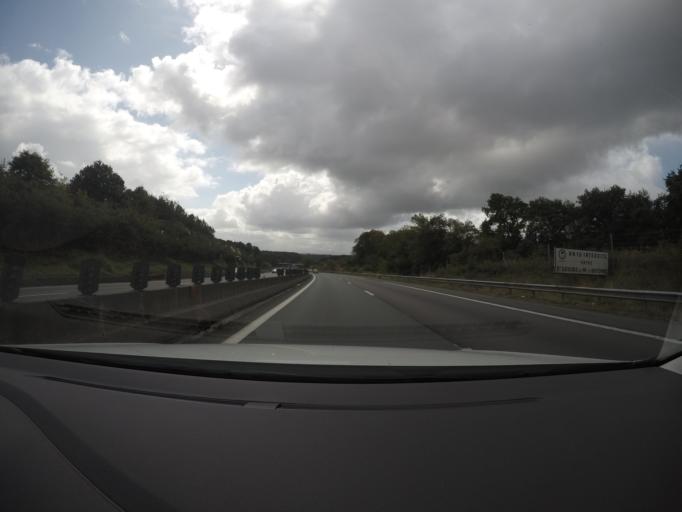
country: FR
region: Aquitaine
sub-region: Departement des Landes
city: Ondres
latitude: 43.5491
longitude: -1.4326
